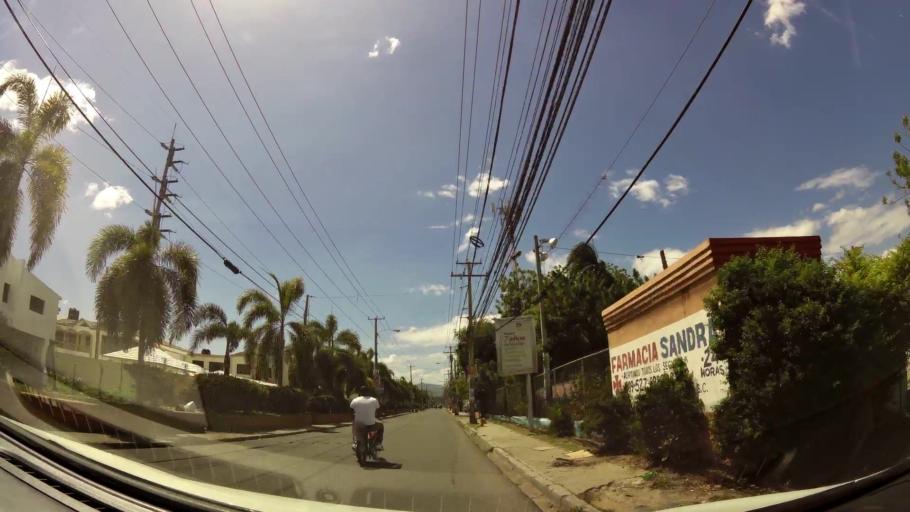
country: DO
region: San Cristobal
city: San Cristobal
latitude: 18.4151
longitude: -70.0985
